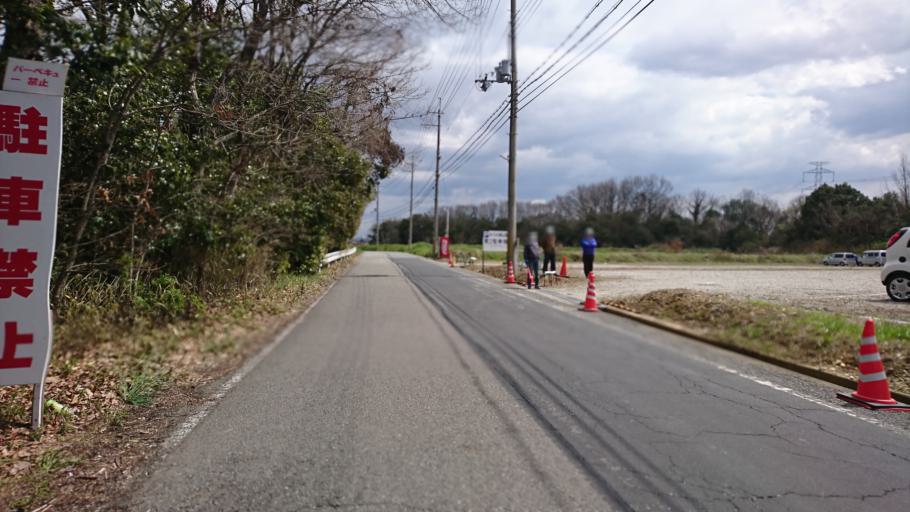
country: JP
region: Hyogo
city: Miki
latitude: 34.7726
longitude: 134.9499
